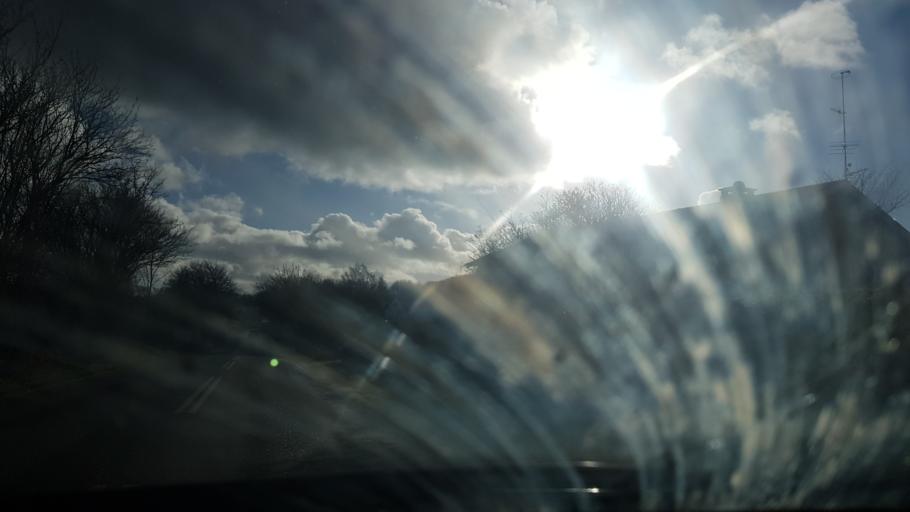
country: DK
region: South Denmark
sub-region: Fredericia Kommune
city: Taulov
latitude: 55.5299
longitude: 9.6388
